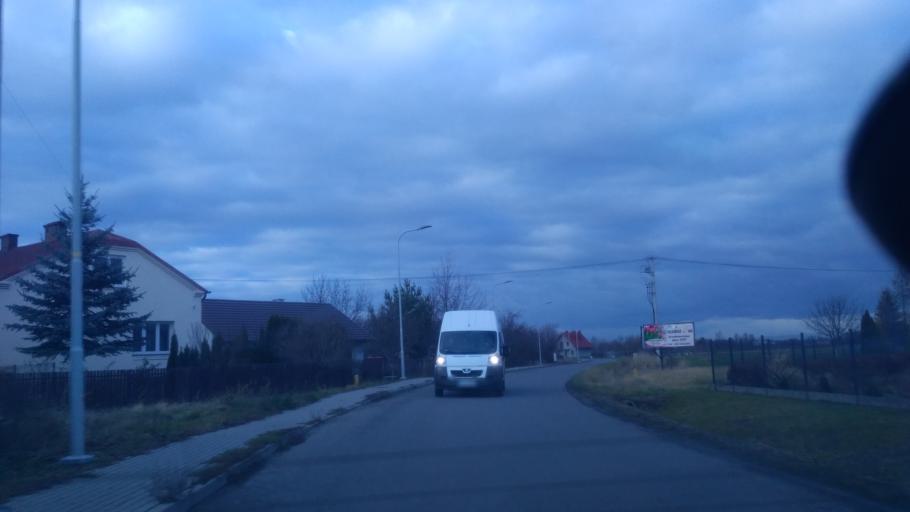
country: PL
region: Subcarpathian Voivodeship
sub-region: Powiat rzeszowski
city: Krasne
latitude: 50.0736
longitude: 22.1121
